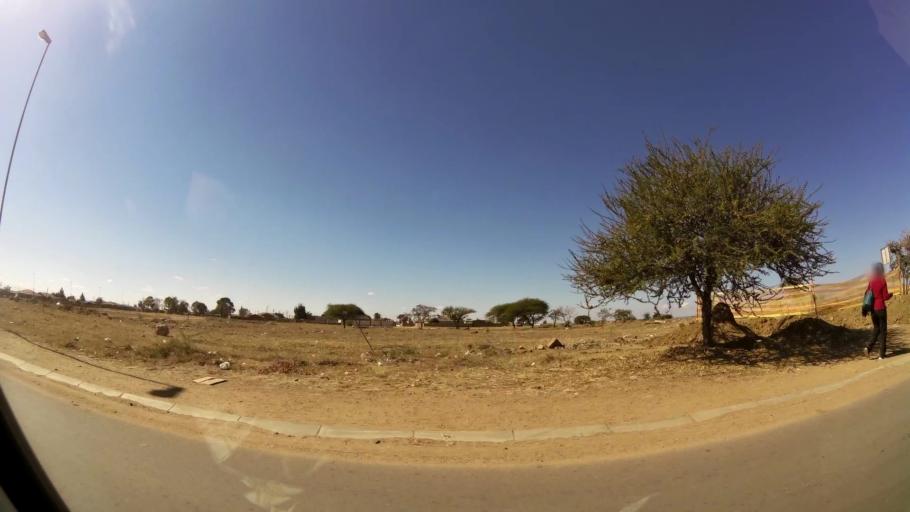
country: ZA
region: Limpopo
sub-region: Capricorn District Municipality
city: Polokwane
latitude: -23.8528
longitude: 29.4127
